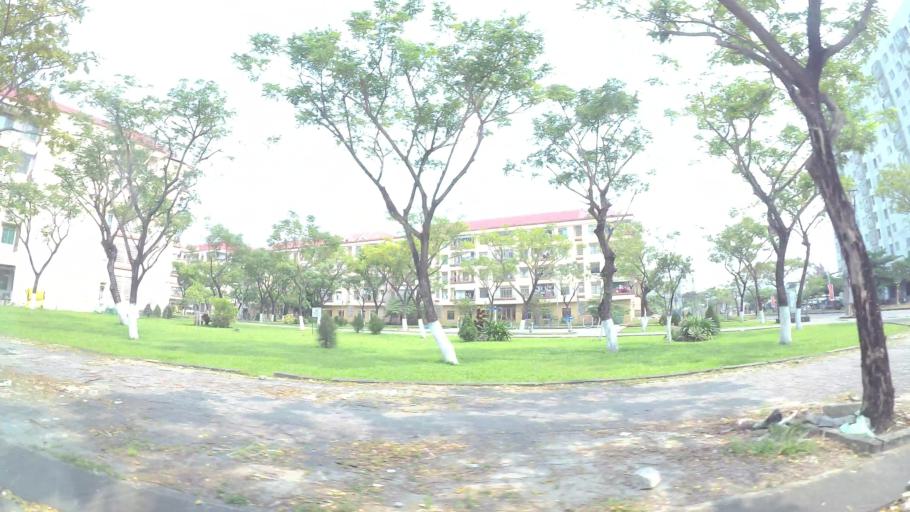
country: VN
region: Da Nang
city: Da Nang
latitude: 16.0906
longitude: 108.2326
